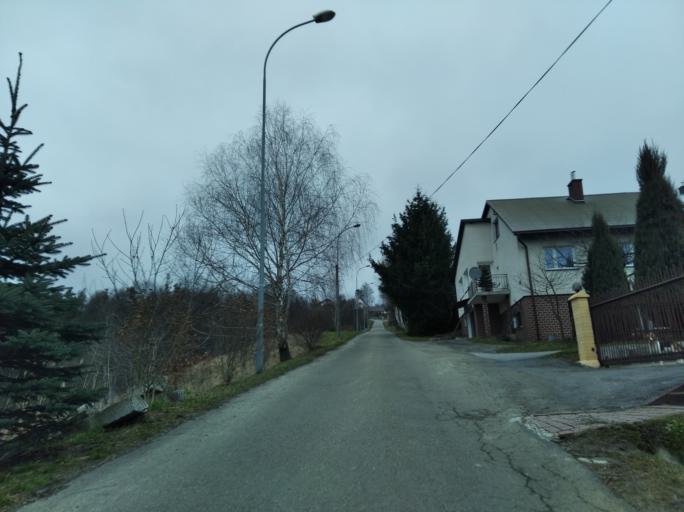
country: PL
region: Subcarpathian Voivodeship
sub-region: Powiat strzyzowski
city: Strzyzow
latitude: 49.8762
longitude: 21.8046
